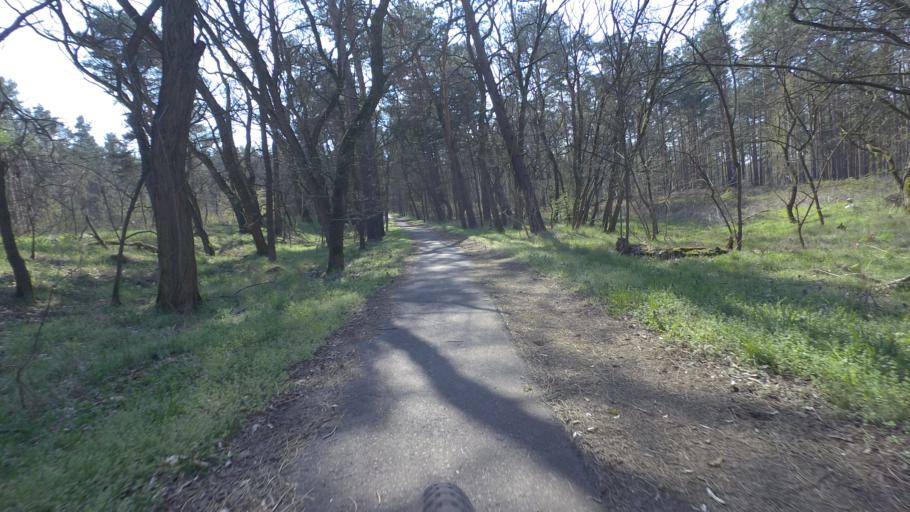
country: DE
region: Brandenburg
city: Mittenwalde
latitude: 52.2092
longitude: 13.5573
